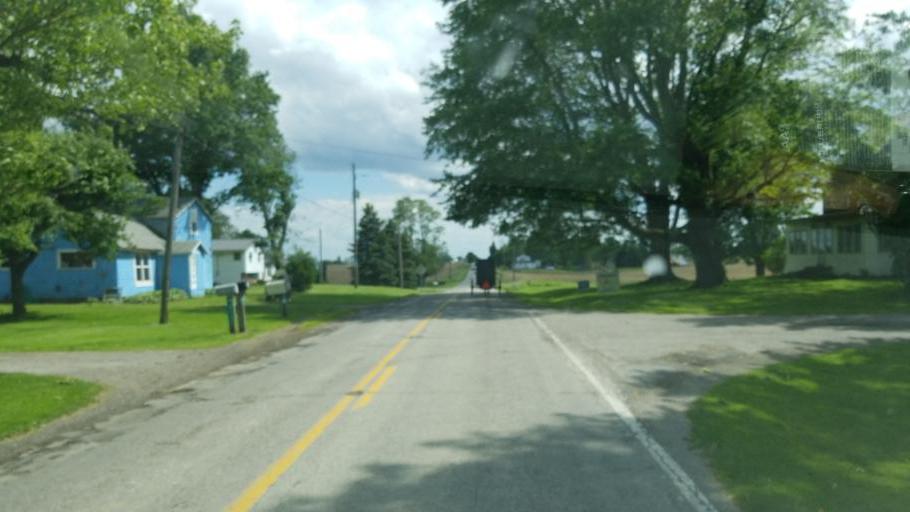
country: US
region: Ohio
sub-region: Huron County
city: Plymouth
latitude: 41.0297
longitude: -82.6077
